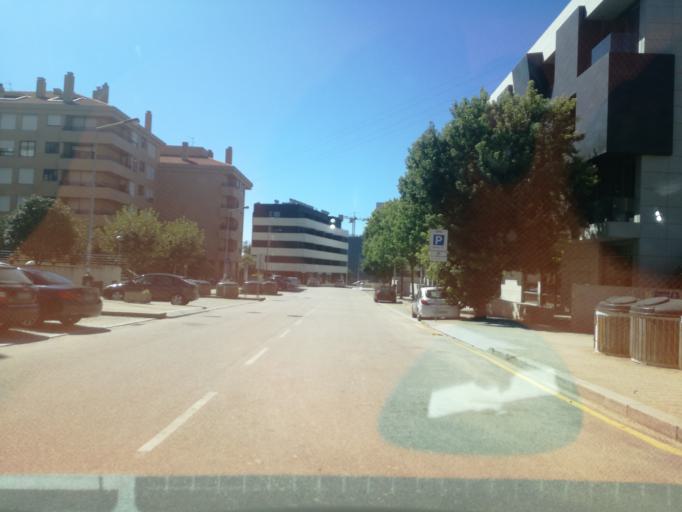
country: PT
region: Porto
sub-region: Matosinhos
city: Sao Mamede de Infesta
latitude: 41.1847
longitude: -8.6026
